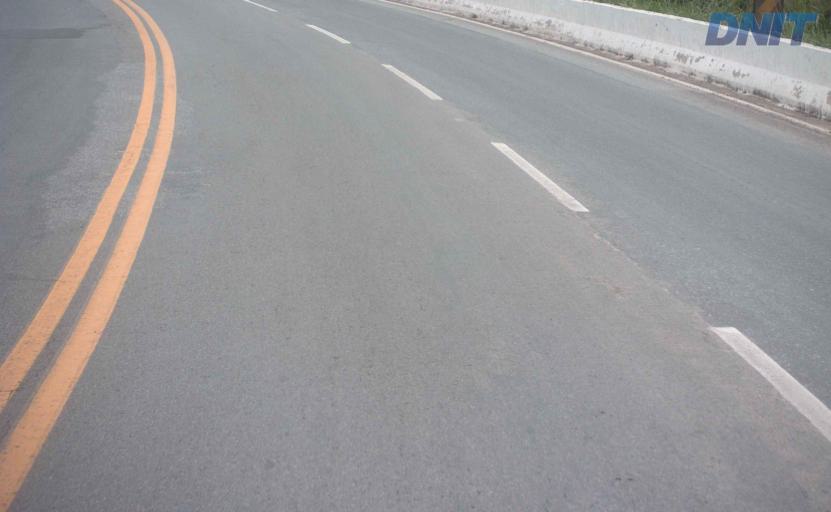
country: BR
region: Minas Gerais
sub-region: Caete
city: Caete
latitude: -19.7361
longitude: -43.5158
